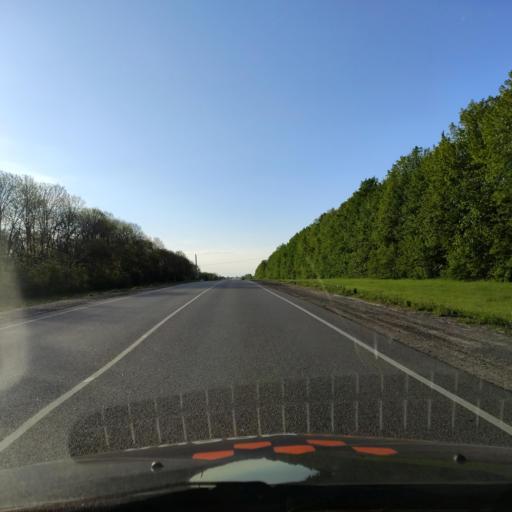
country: RU
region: Lipetsk
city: Yelets
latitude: 52.5688
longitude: 38.6659
